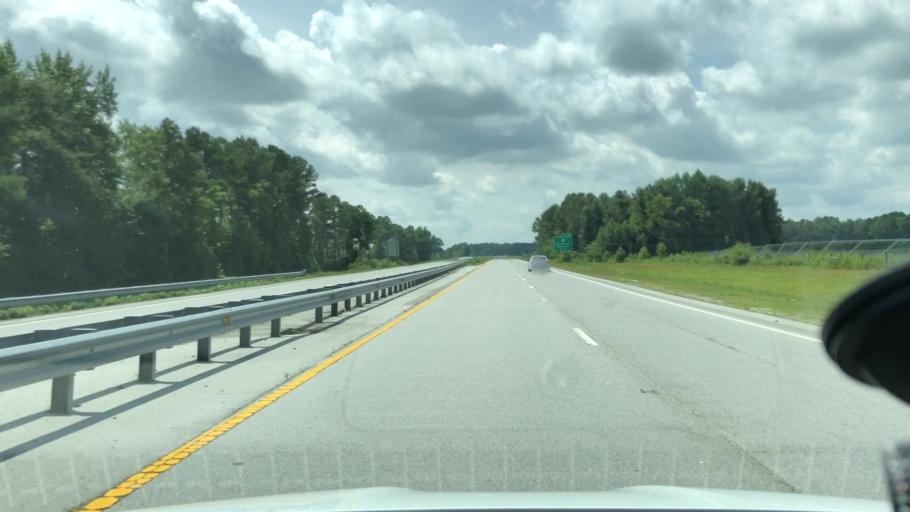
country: US
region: North Carolina
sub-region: Beaufort County
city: Washington
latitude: 35.5181
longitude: -77.0858
